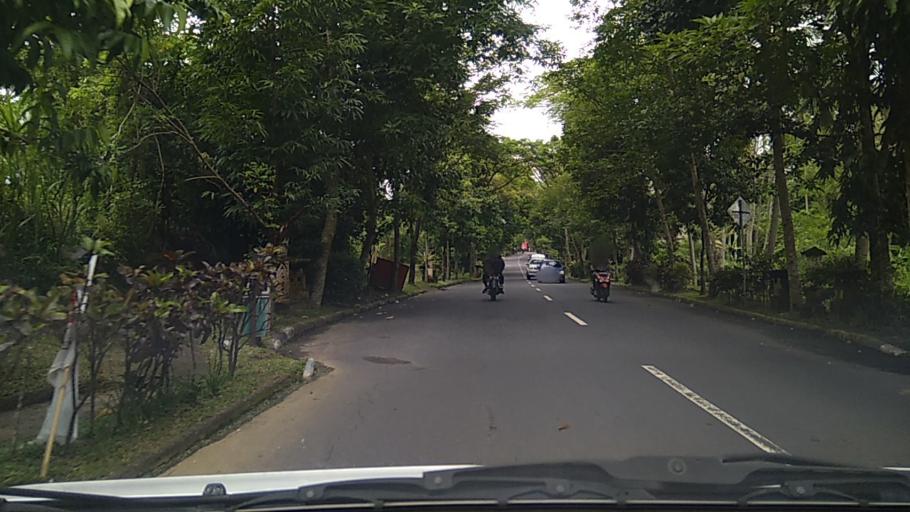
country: ID
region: Bali
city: Banjar Kelodan
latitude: -8.5232
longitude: 115.3463
